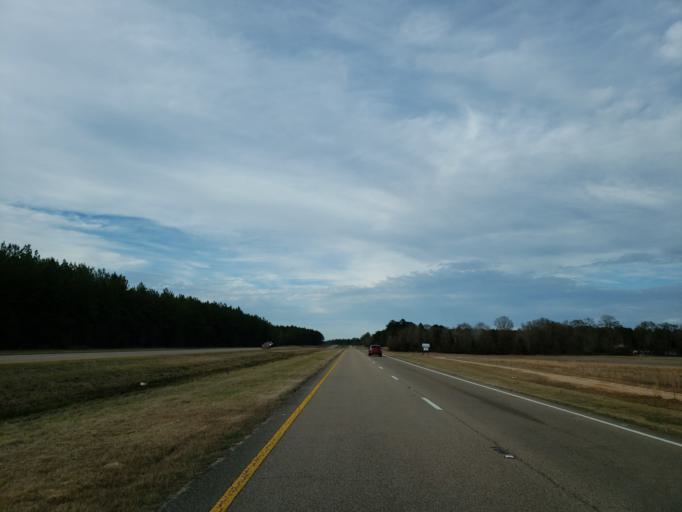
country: US
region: Mississippi
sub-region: Wayne County
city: Waynesboro
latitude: 31.6380
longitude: -88.5936
